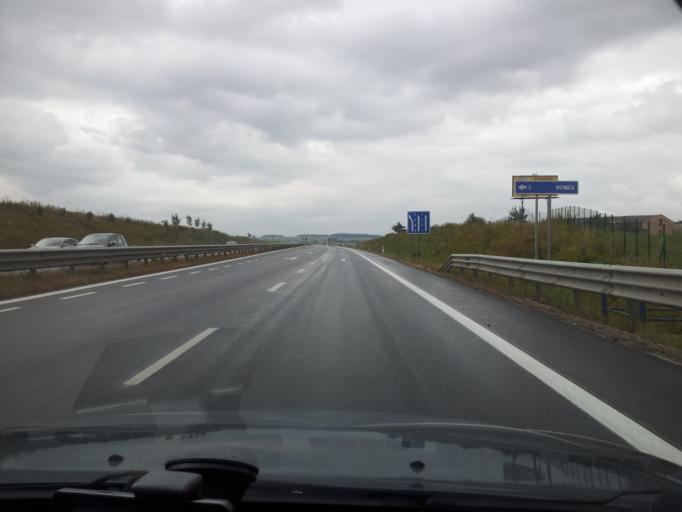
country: SK
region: Presovsky
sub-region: Okres Poprad
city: Poprad
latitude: 49.0961
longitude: 20.3404
